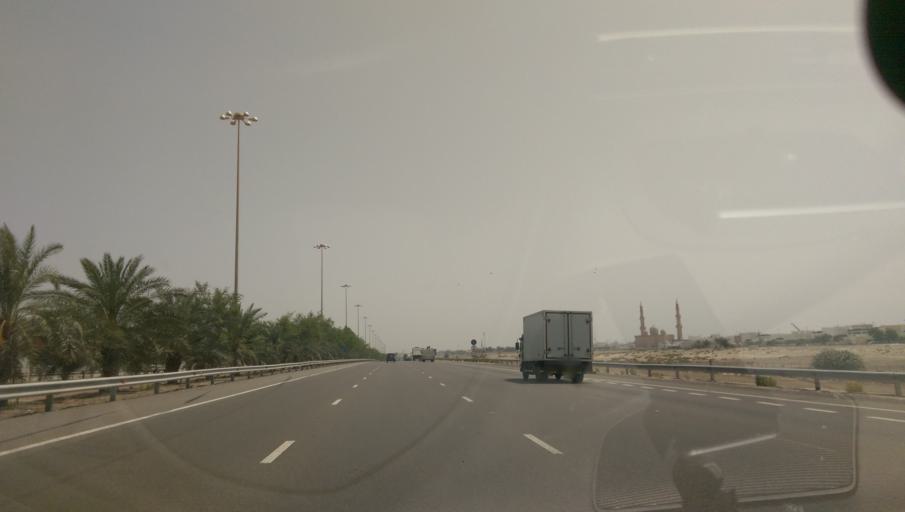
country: AE
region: Abu Dhabi
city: Abu Dhabi
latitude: 24.3469
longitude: 54.6412
